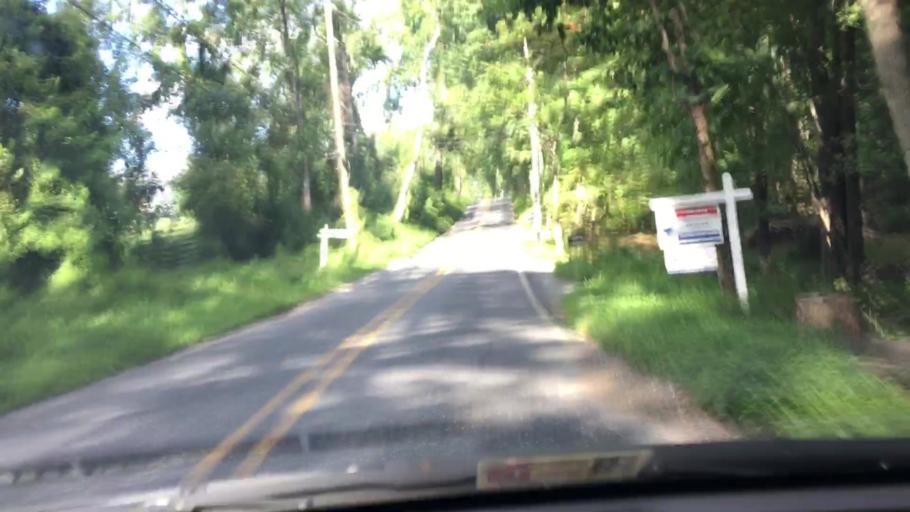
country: US
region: Maryland
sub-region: Montgomery County
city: Montgomery Village
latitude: 39.2090
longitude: -77.2130
